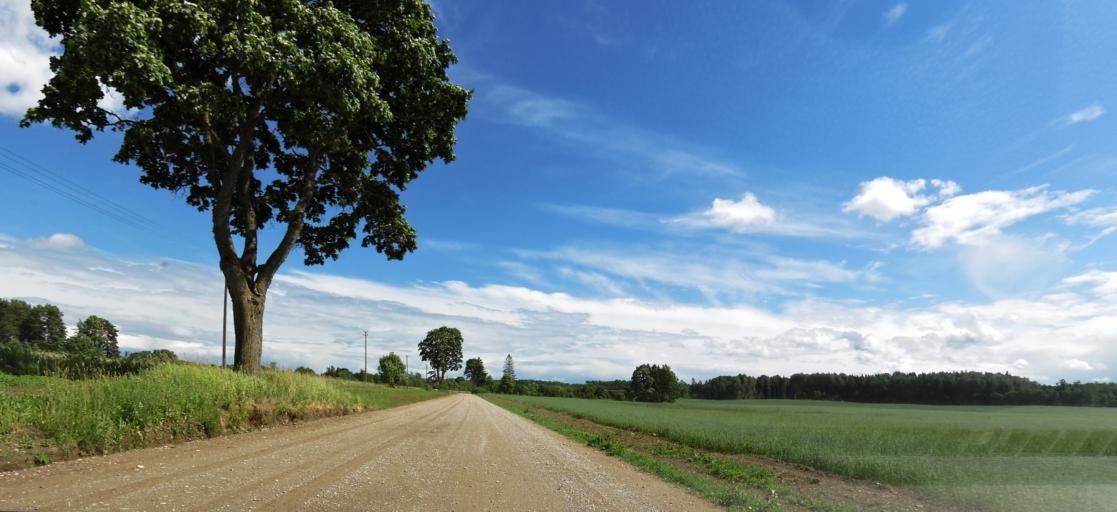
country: LT
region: Panevezys
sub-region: Birzai
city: Birzai
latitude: 56.4118
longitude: 24.8156
